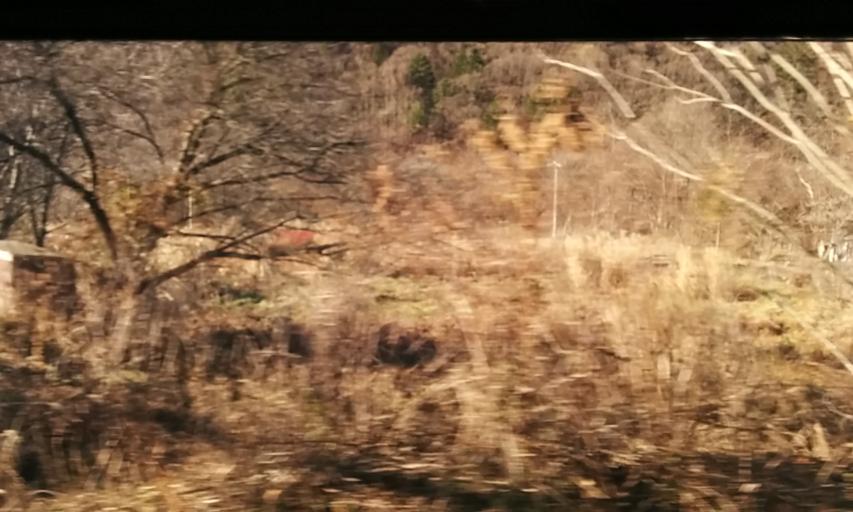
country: JP
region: Nagano
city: Ina
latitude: 35.8728
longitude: 137.7450
